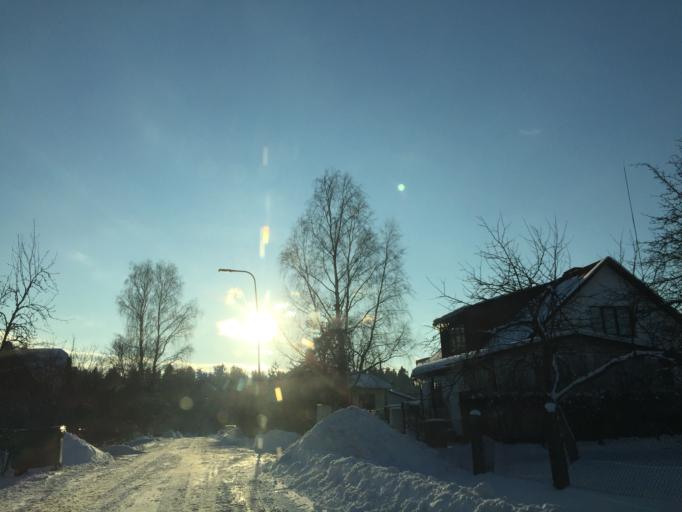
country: LV
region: Incukalns
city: Incukalns
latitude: 57.1053
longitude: 24.6777
